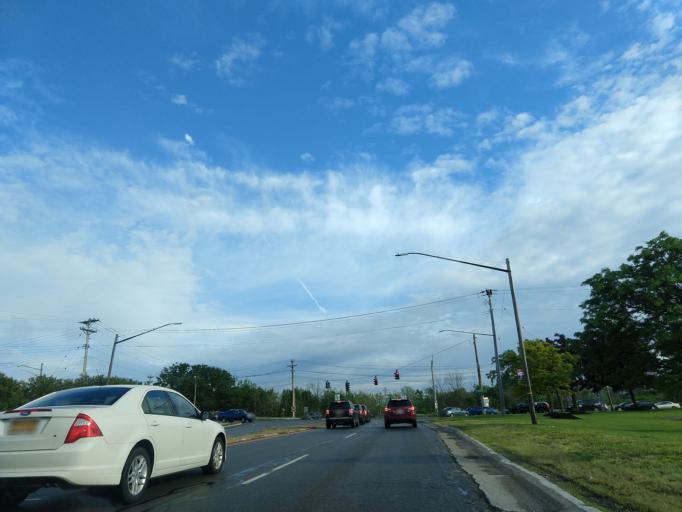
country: US
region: New York
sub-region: Erie County
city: West Seneca
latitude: 42.8293
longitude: -78.7881
